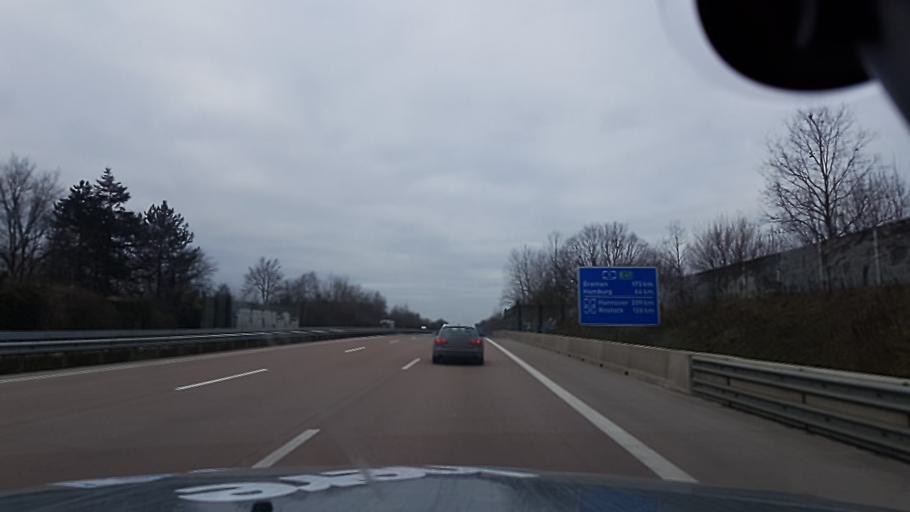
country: DE
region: Schleswig-Holstein
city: Stockelsdorf
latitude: 53.8739
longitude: 10.6492
